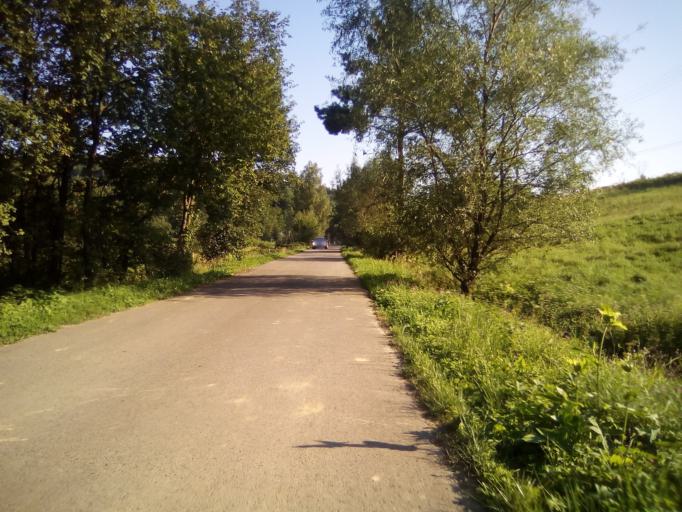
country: PL
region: Subcarpathian Voivodeship
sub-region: Powiat brzozowski
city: Domaradz
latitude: 49.8115
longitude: 21.9446
